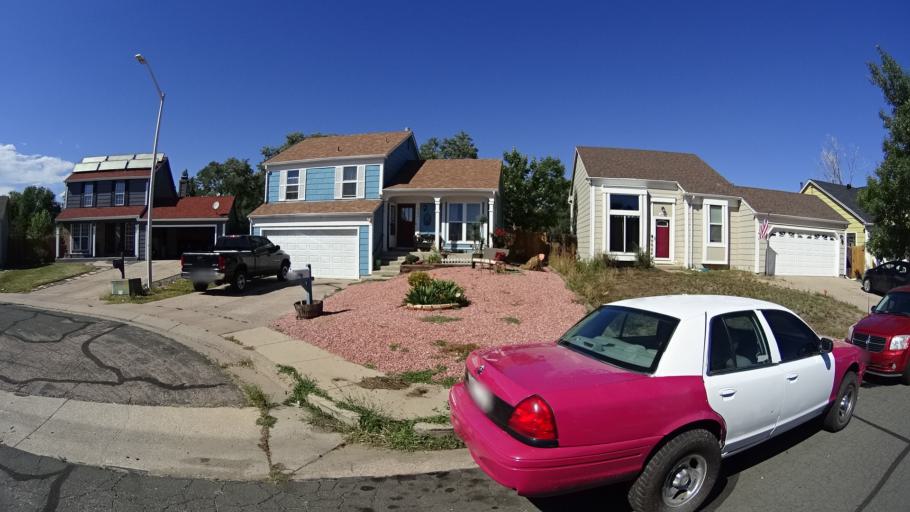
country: US
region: Colorado
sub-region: El Paso County
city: Stratmoor
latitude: 38.7959
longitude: -104.7382
